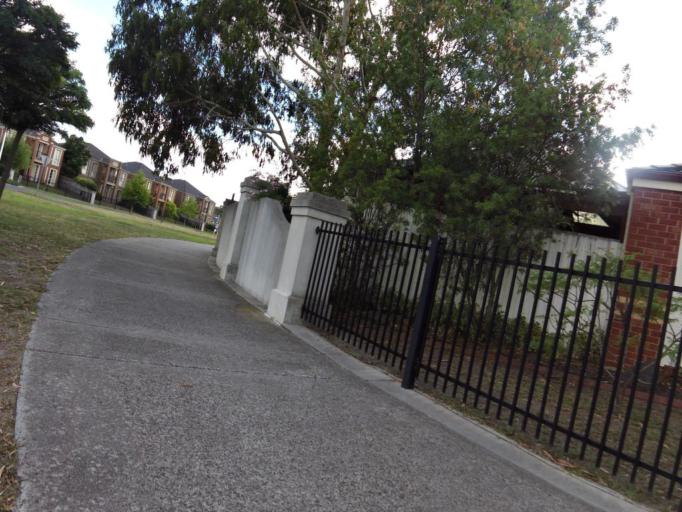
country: AU
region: Victoria
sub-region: Whittlesea
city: Mill Park
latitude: -37.6311
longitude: 145.0682
